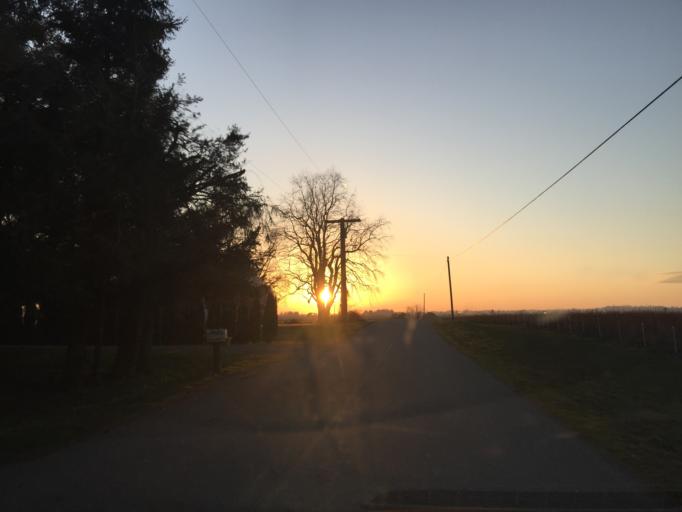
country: US
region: Washington
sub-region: Whatcom County
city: Sumas
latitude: 48.9863
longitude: -122.2002
